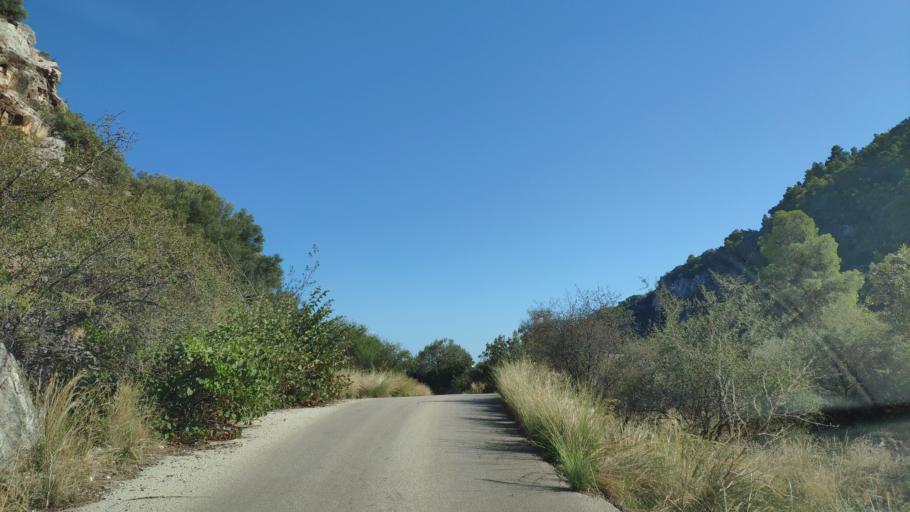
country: GR
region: Peloponnese
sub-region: Nomos Korinthias
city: Sofikon
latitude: 37.7336
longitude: 23.1127
